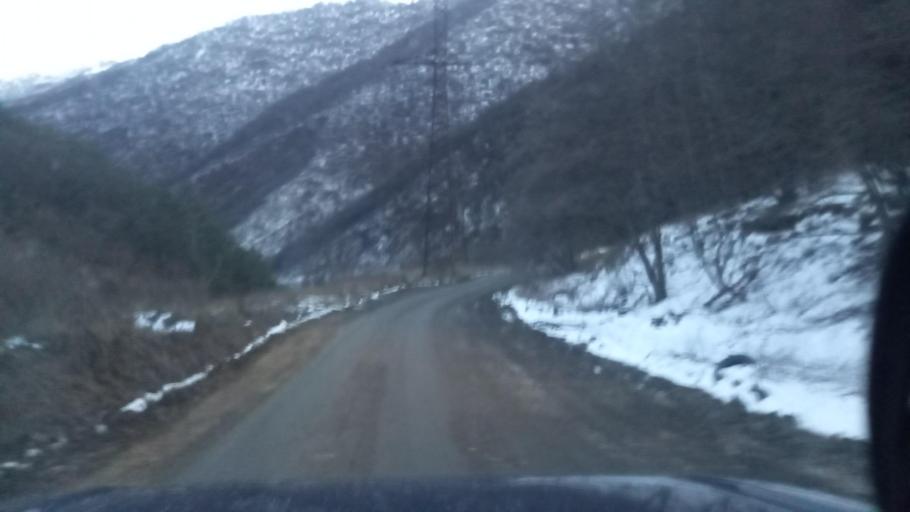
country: RU
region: Ingushetiya
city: Dzhayrakh
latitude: 42.8285
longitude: 44.5885
